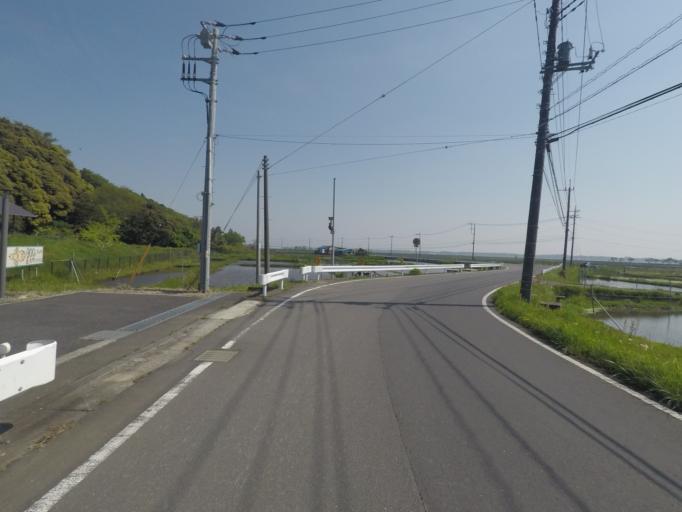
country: JP
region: Ibaraki
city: Ami
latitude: 36.0759
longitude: 140.2460
